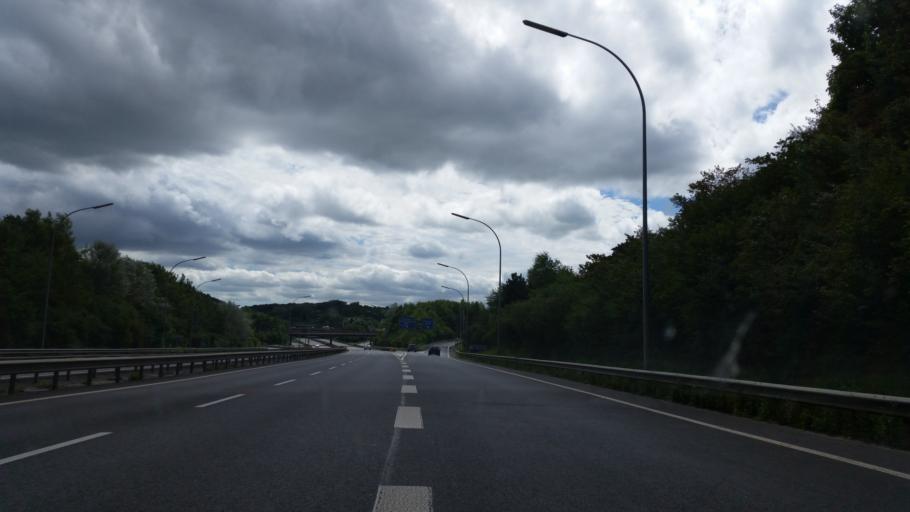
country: LU
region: Luxembourg
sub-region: Canton de Luxembourg
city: Strassen
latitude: 49.5916
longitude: 6.0881
